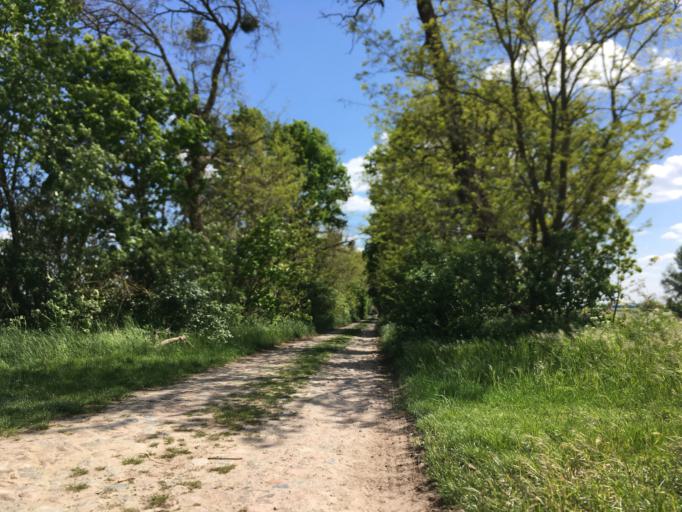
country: DE
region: Brandenburg
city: Werneuchen
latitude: 52.6662
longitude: 13.6754
